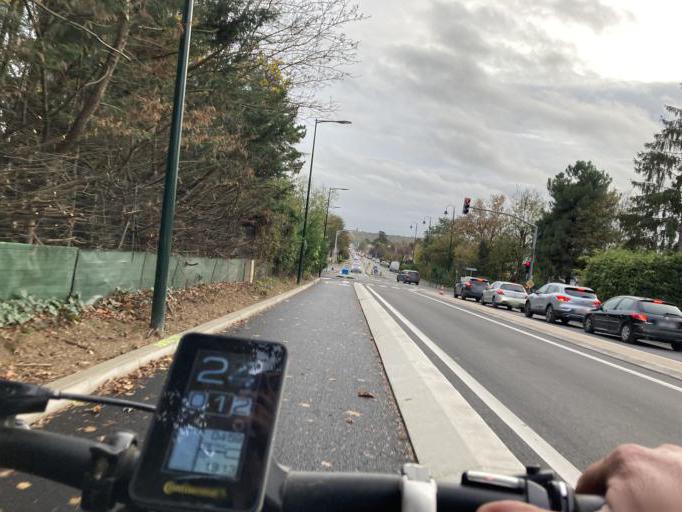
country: FR
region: Picardie
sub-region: Departement de l'Oise
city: Lamorlaye
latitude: 49.1603
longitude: 2.4474
